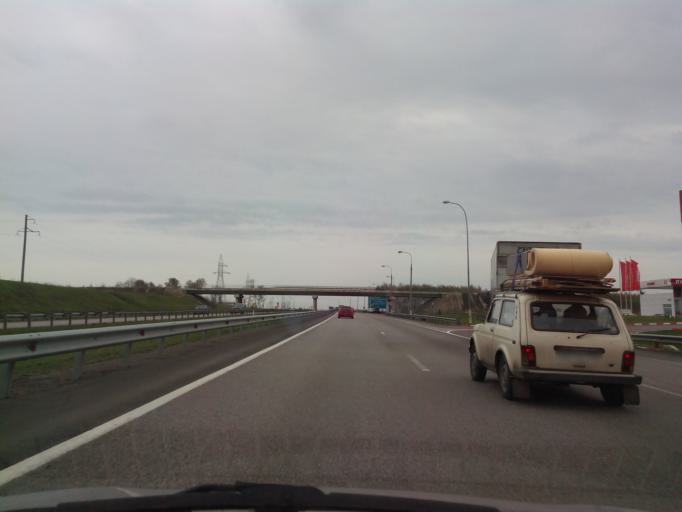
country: RU
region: Moskovskaya
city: Kashira
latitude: 54.7890
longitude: 38.1041
